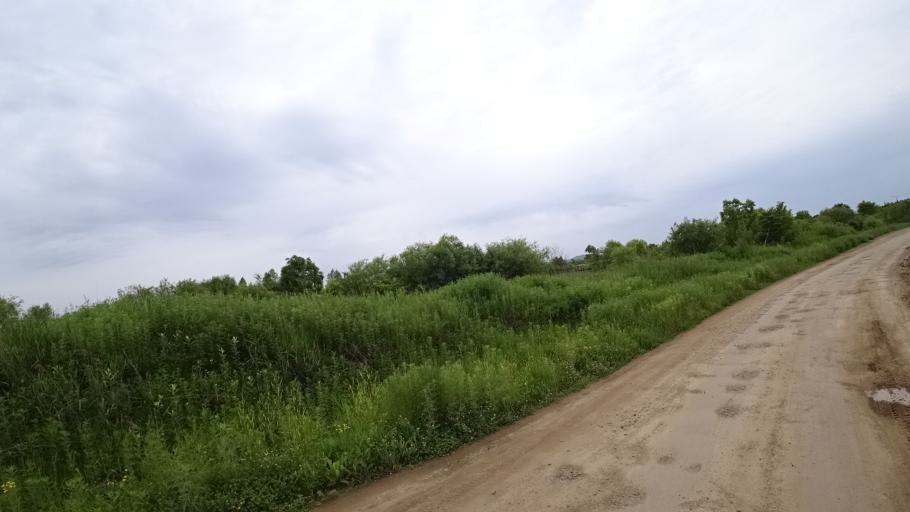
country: RU
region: Primorskiy
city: Arsen'yev
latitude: 44.1986
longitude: 133.3092
